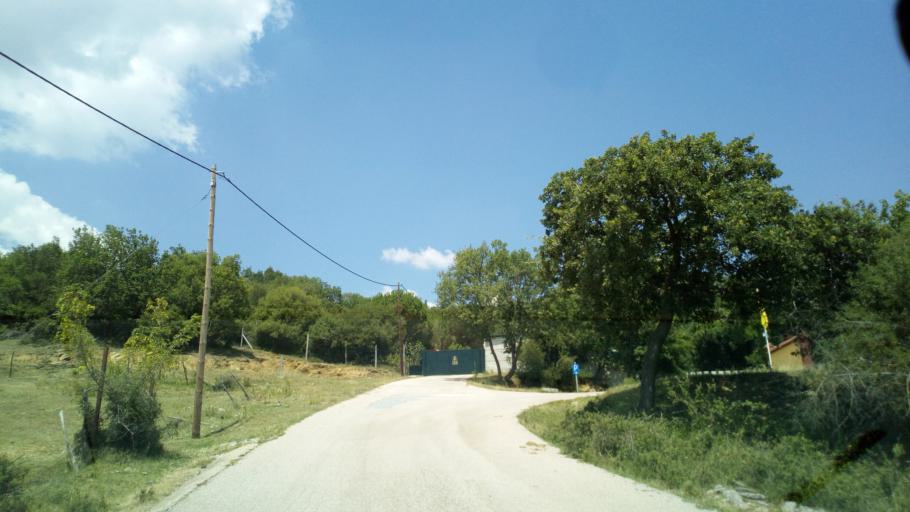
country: GR
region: Central Macedonia
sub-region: Nomos Thessalonikis
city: Sochos
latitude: 40.8183
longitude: 23.3419
